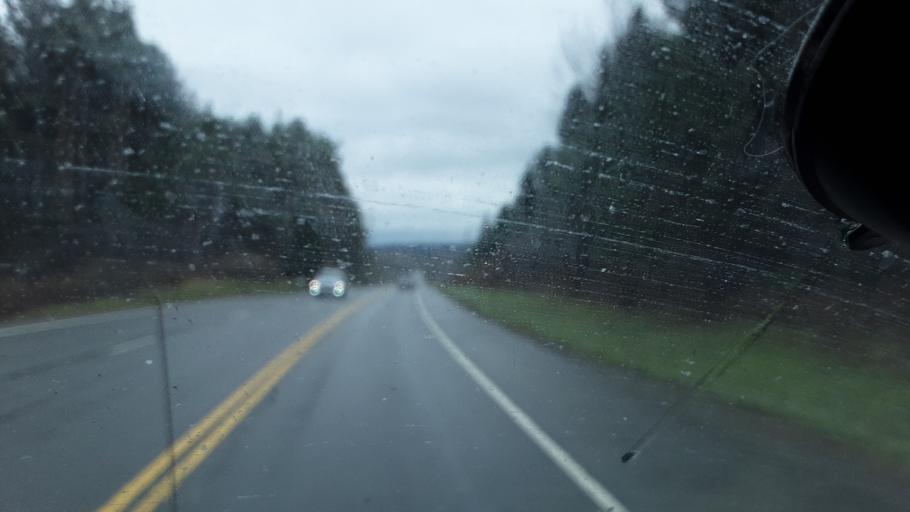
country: US
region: New York
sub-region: Cattaraugus County
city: Yorkshire
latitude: 42.5910
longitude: -78.4950
